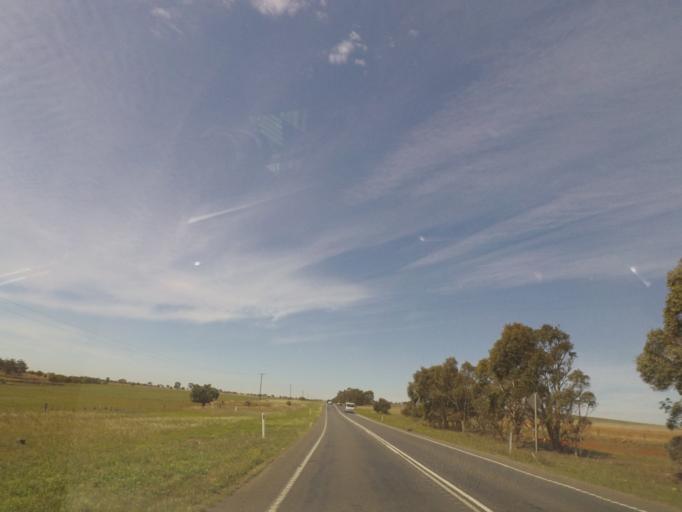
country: AU
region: Victoria
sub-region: Moorabool
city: Bacchus Marsh
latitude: -37.7559
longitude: 144.4418
